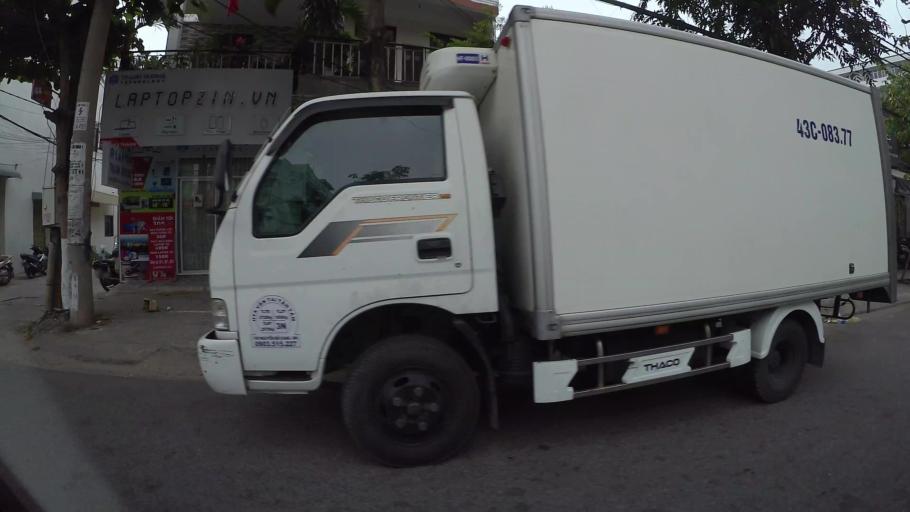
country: VN
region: Da Nang
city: Cam Le
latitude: 16.0314
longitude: 108.2227
